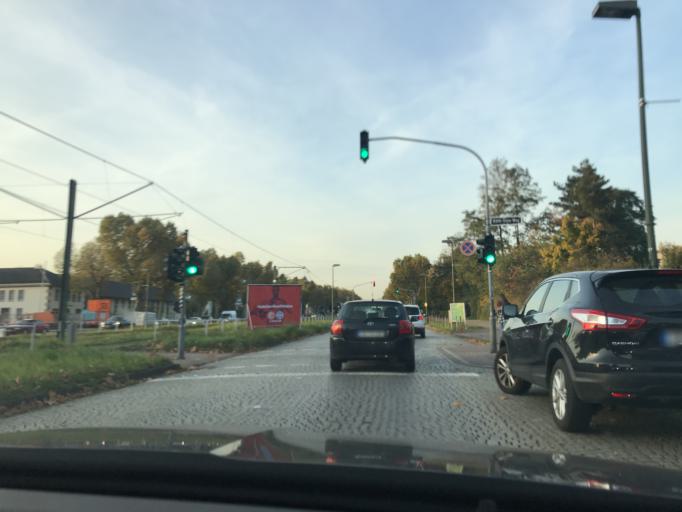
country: DE
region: North Rhine-Westphalia
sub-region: Regierungsbezirk Dusseldorf
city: Dusseldorf
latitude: 51.2569
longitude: 6.7557
